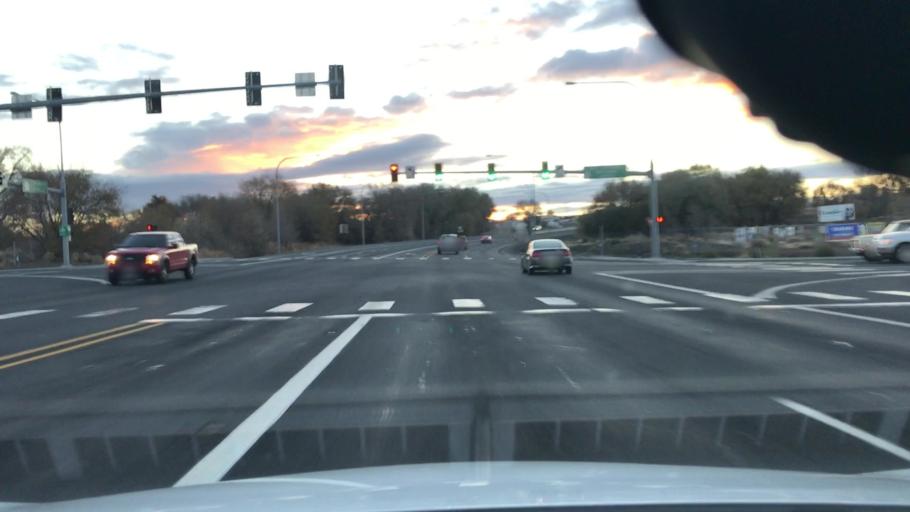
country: US
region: Washington
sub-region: Grant County
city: Moses Lake
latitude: 47.1398
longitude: -119.2627
